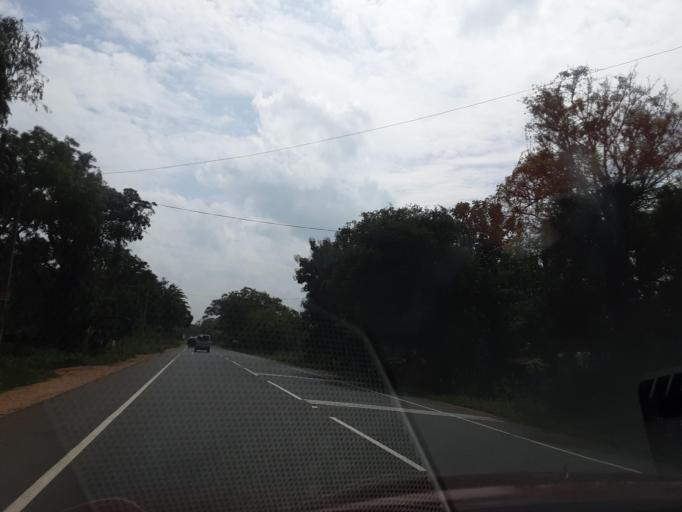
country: LK
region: North Central
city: Anuradhapura
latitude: 8.5008
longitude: 80.5122
